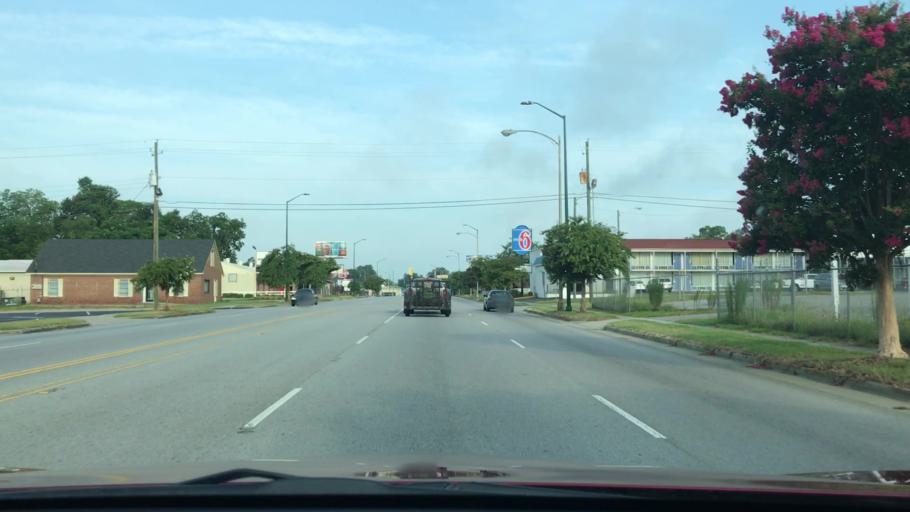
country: US
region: South Carolina
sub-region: Orangeburg County
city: Orangeburg
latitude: 33.4909
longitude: -80.8507
